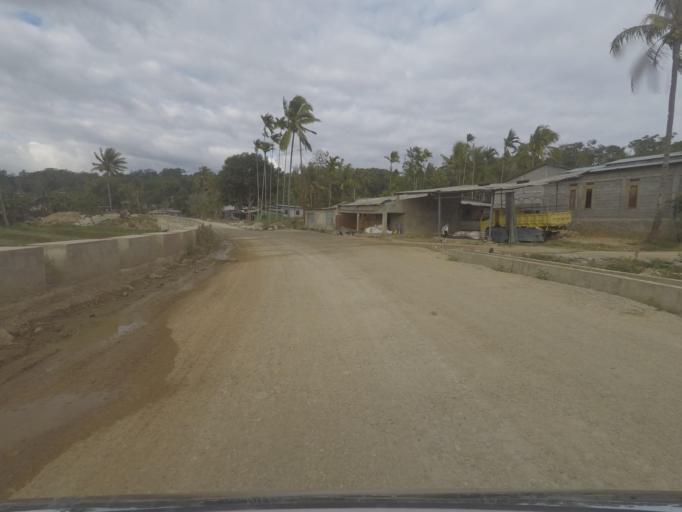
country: TL
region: Baucau
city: Venilale
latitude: -8.5930
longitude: 126.3854
